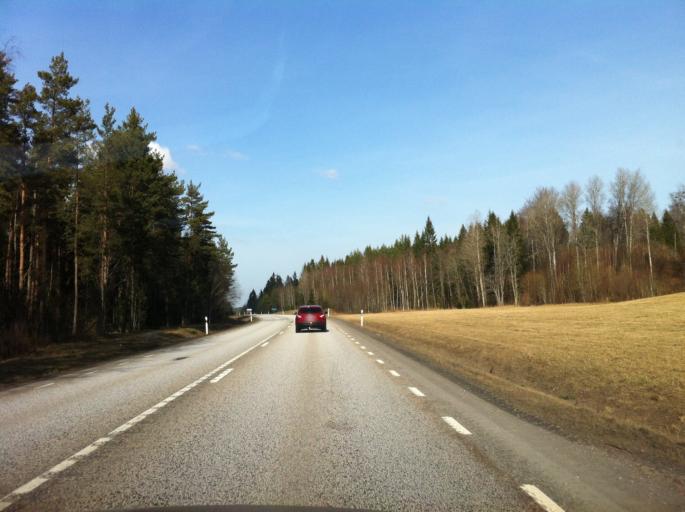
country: SE
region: Joenkoeping
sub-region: Mullsjo Kommun
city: Mullsjoe
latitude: 57.9587
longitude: 13.8322
